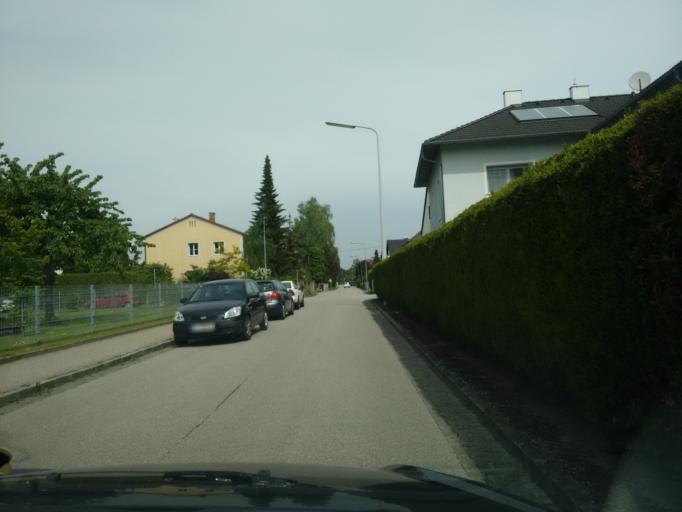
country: AT
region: Upper Austria
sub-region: Politischer Bezirk Linz-Land
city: Traun
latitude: 48.2282
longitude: 14.2473
